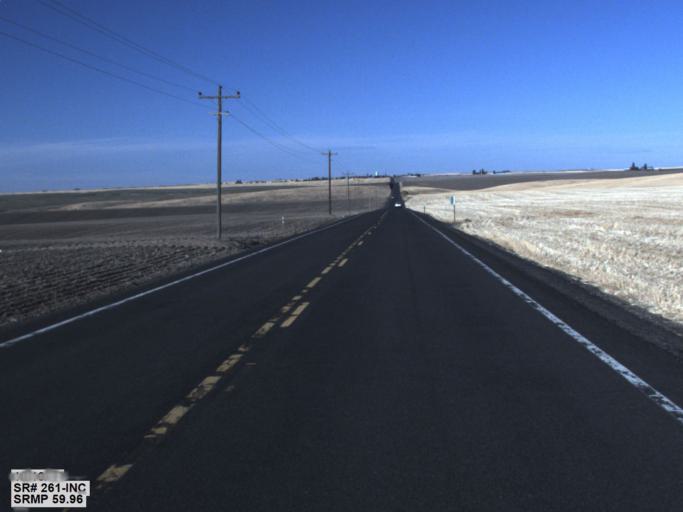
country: US
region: Washington
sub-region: Adams County
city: Ritzville
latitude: 47.0755
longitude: -118.3654
